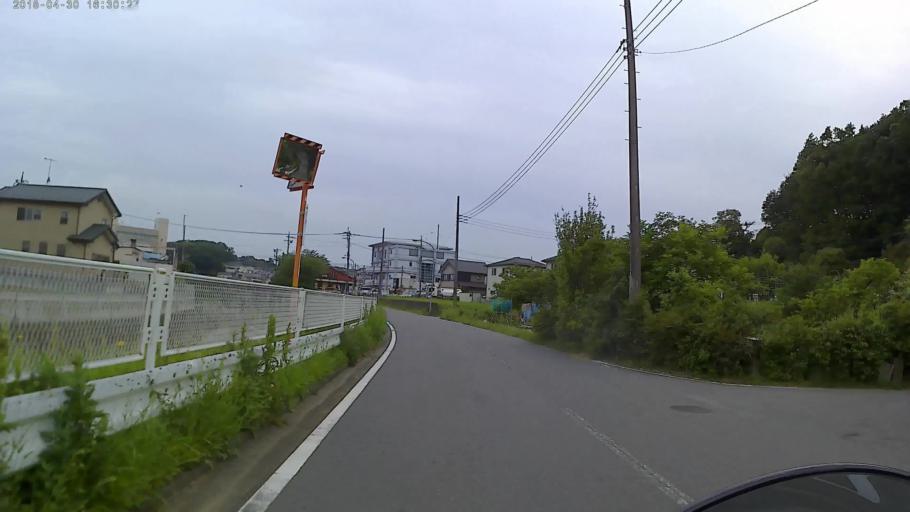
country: JP
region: Kanagawa
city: Zama
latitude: 35.4539
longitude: 139.4035
